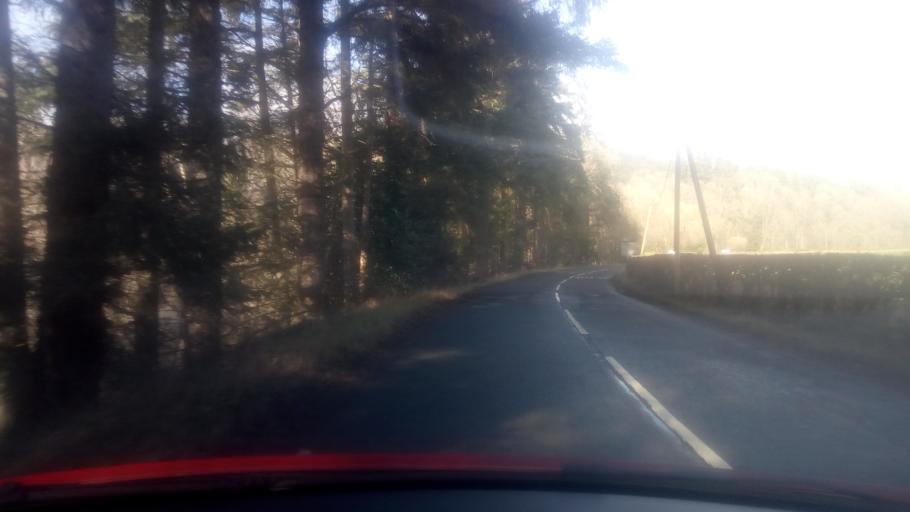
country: GB
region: Scotland
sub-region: The Scottish Borders
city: Selkirk
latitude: 55.5867
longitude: -2.8669
